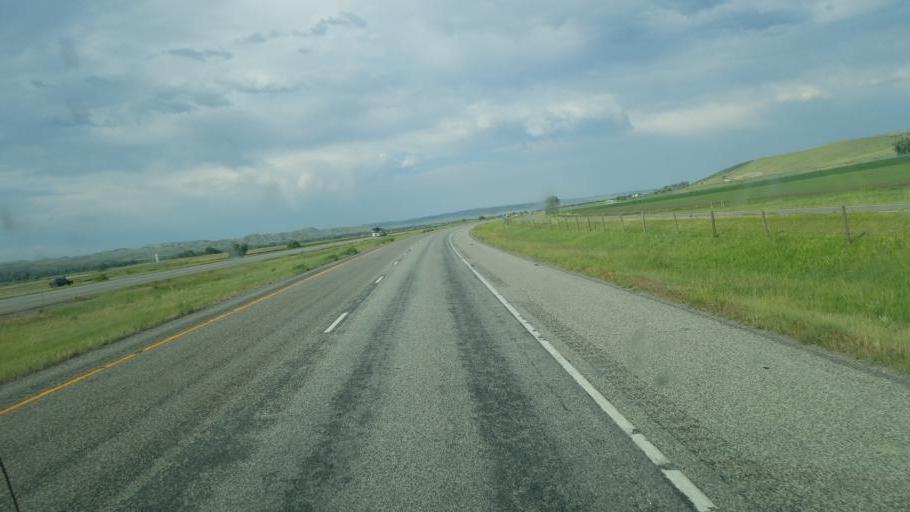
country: US
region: Montana
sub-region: Sweet Grass County
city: Big Timber
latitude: 45.8040
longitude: -110.0215
